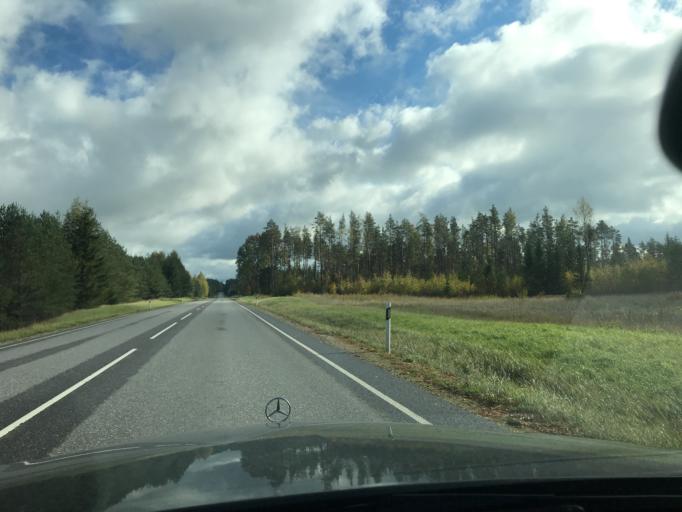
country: EE
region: Vorumaa
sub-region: Voru linn
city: Voru
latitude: 57.7688
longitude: 27.1628
